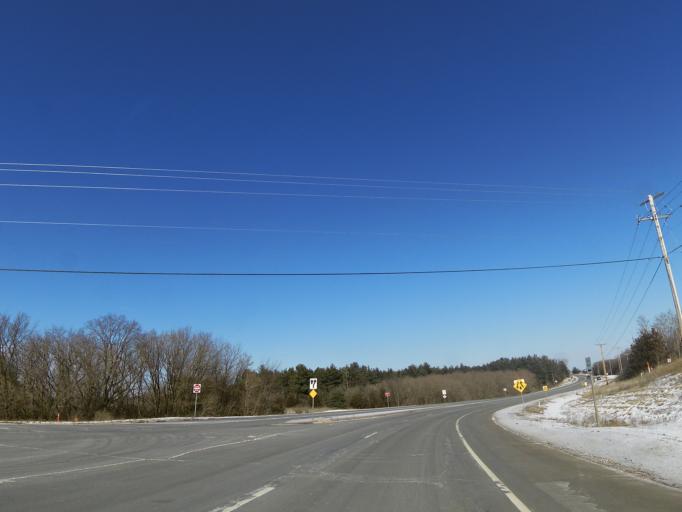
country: US
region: Wisconsin
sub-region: Saint Croix County
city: North Hudson
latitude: 44.9919
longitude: -92.6803
